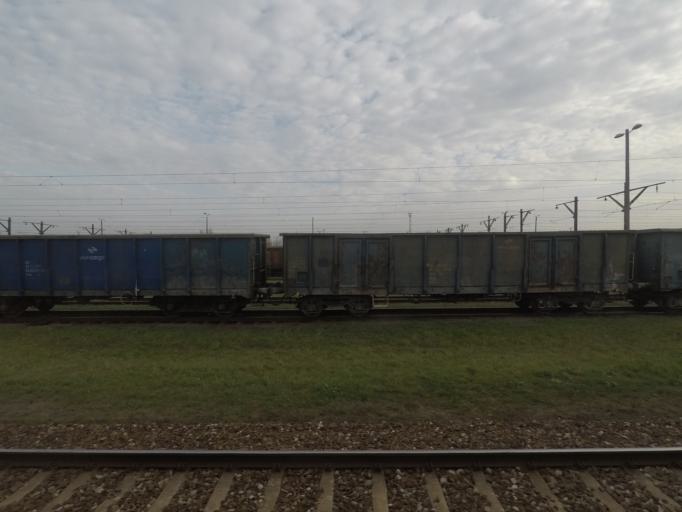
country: PL
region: Subcarpathian Voivodeship
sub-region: Powiat przemyski
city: Orly
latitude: 49.8385
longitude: 22.8419
